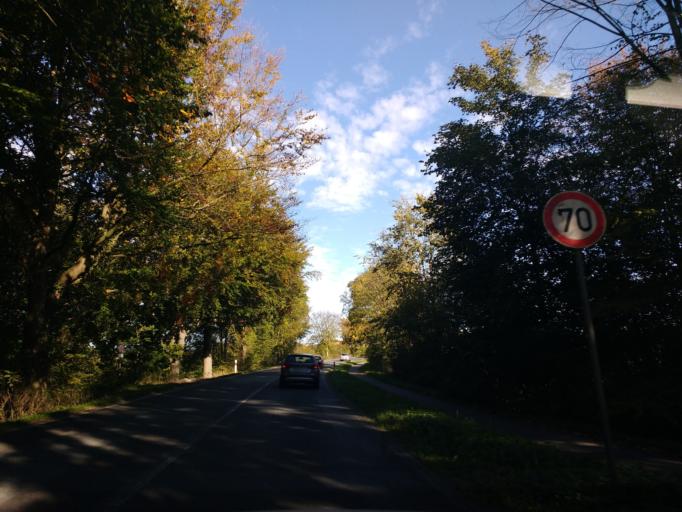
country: DE
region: Schleswig-Holstein
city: Ratekau
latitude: 53.9630
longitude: 10.7597
